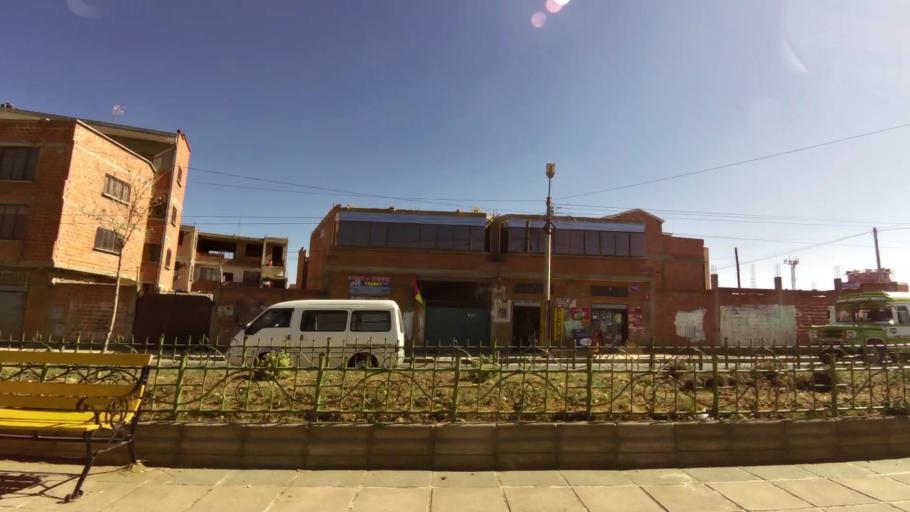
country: BO
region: La Paz
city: La Paz
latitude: -16.5197
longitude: -68.1874
